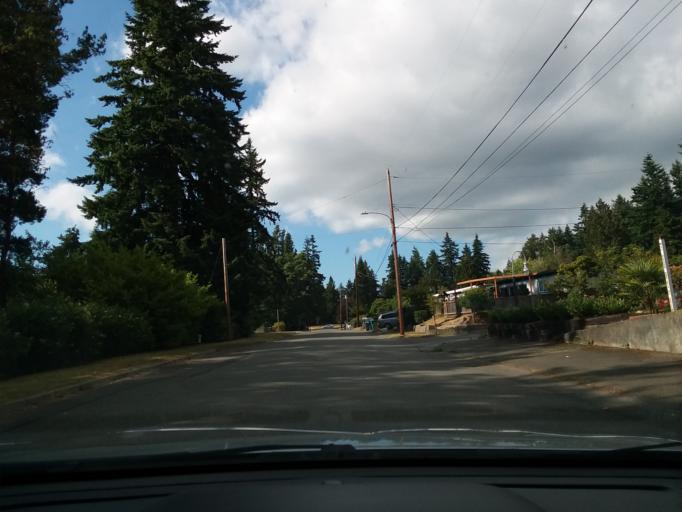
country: US
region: Washington
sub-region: Snohomish County
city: Mountlake Terrace
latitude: 47.7867
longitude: -122.3193
